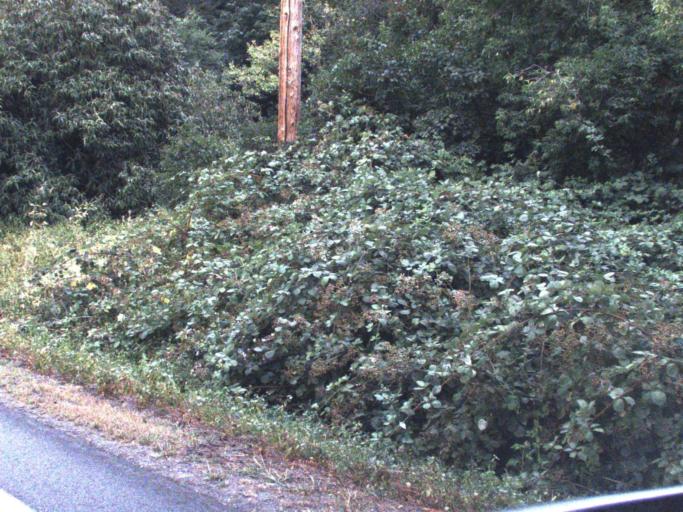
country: US
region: Washington
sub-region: King County
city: Union Hill-Novelty Hill
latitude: 47.6504
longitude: -122.0461
